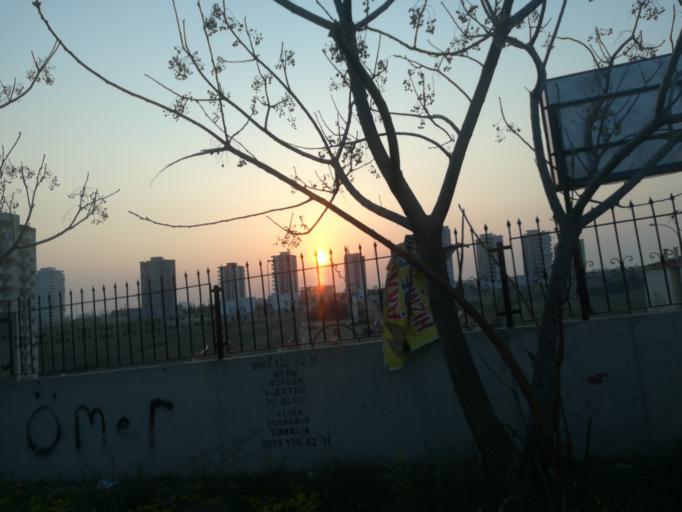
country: TR
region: Adana
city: Adana
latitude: 37.0782
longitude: 35.4145
